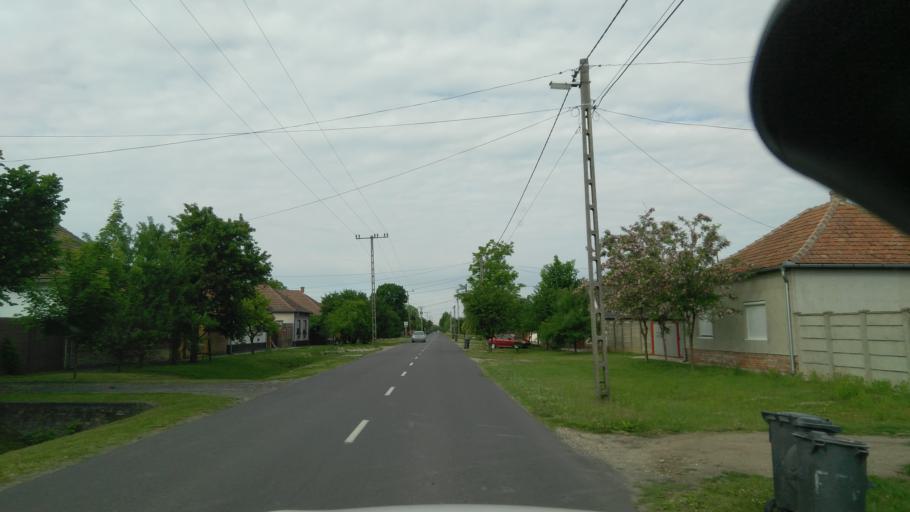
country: HU
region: Bekes
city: Ketegyhaza
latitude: 46.5444
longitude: 21.1759
